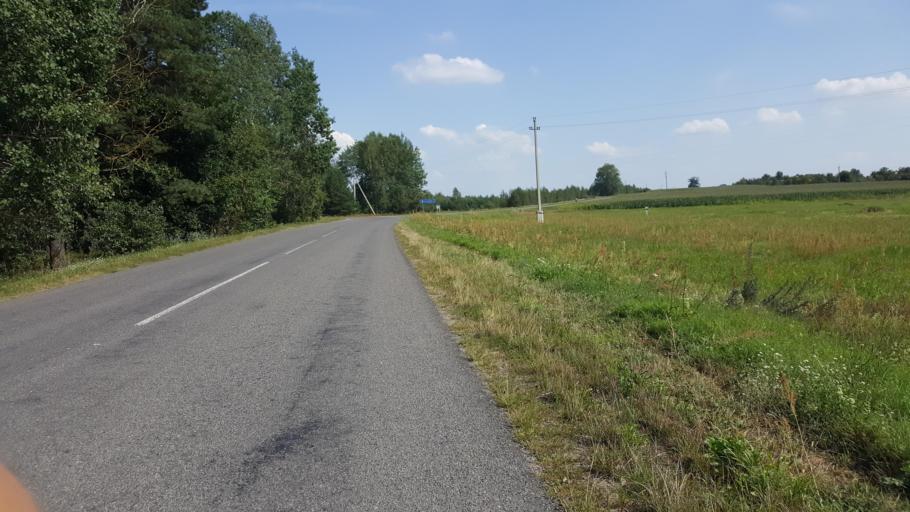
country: BY
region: Brest
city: Kamyanyuki
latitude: 52.5038
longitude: 23.6596
